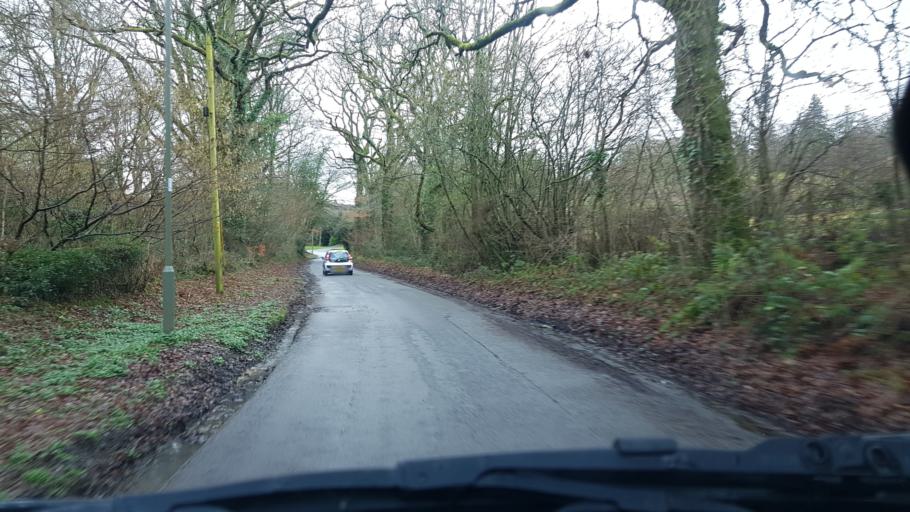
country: GB
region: England
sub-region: Surrey
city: Haslemere
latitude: 51.0969
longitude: -0.6887
